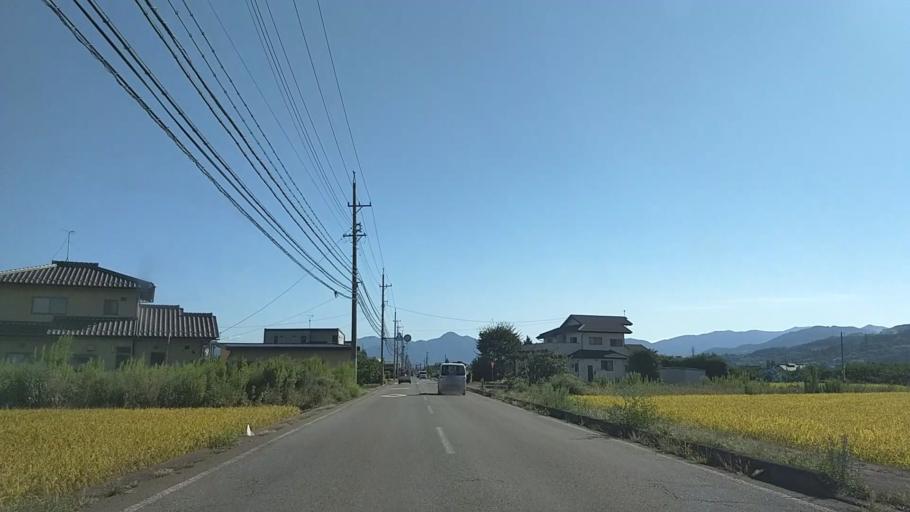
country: JP
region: Nagano
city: Nagano-shi
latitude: 36.6072
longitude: 138.1433
